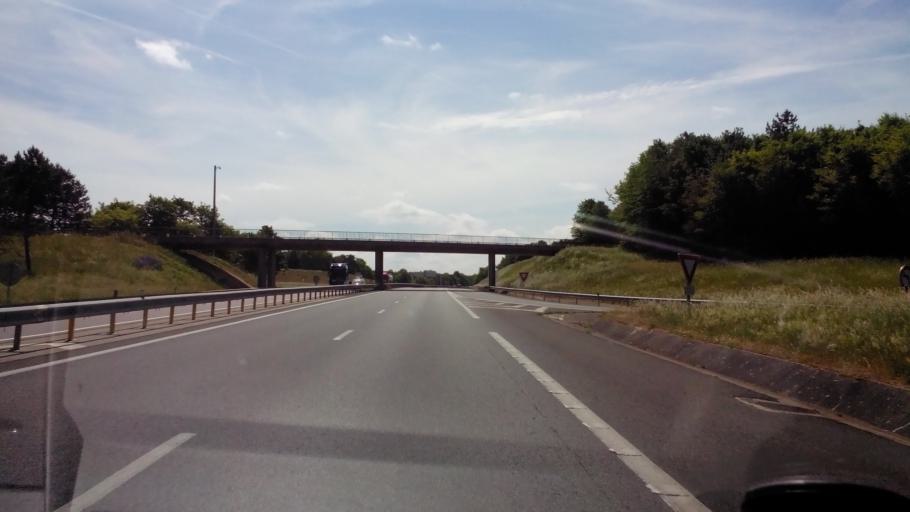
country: FR
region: Lorraine
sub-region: Departement de Meurthe-et-Moselle
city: Colombey-les-Belles
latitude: 48.5376
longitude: 5.9054
